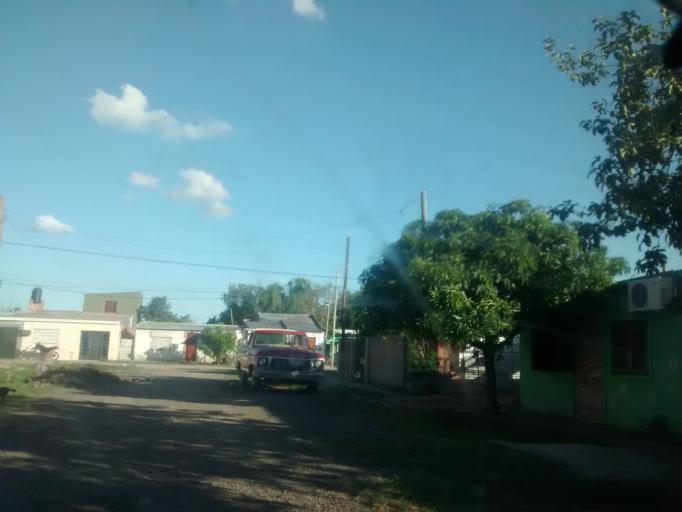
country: AR
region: Chaco
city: Fontana
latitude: -27.4507
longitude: -59.0203
